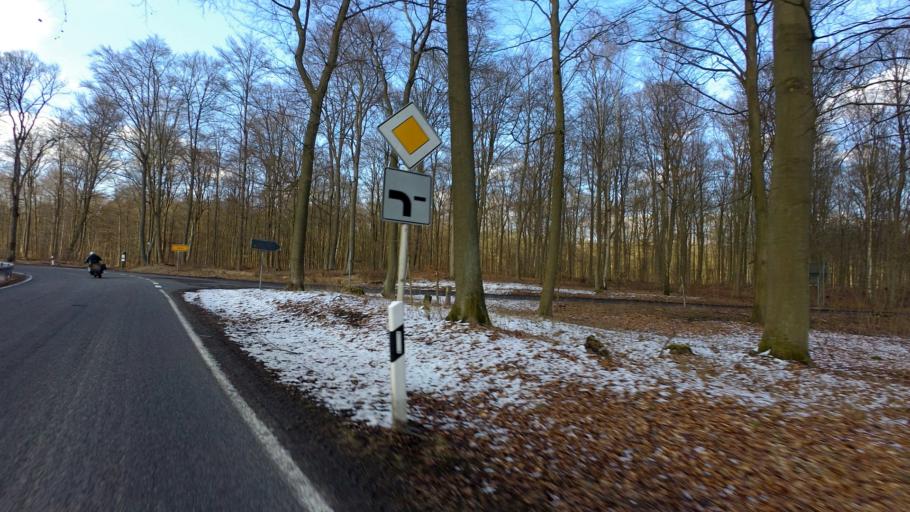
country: DE
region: Brandenburg
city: Wandlitz
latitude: 52.7689
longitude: 13.5142
